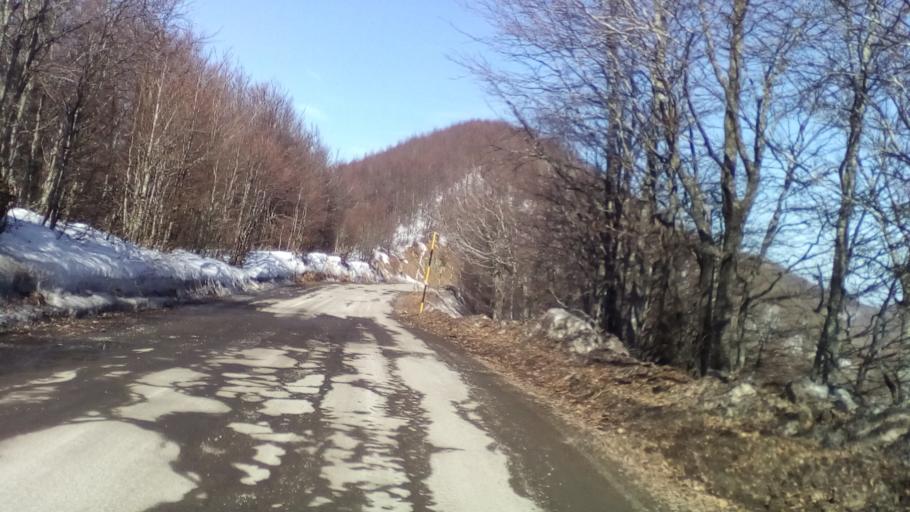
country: IT
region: Tuscany
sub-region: Provincia di Lucca
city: Castiglione di Garfagnana
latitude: 44.2013
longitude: 10.4880
